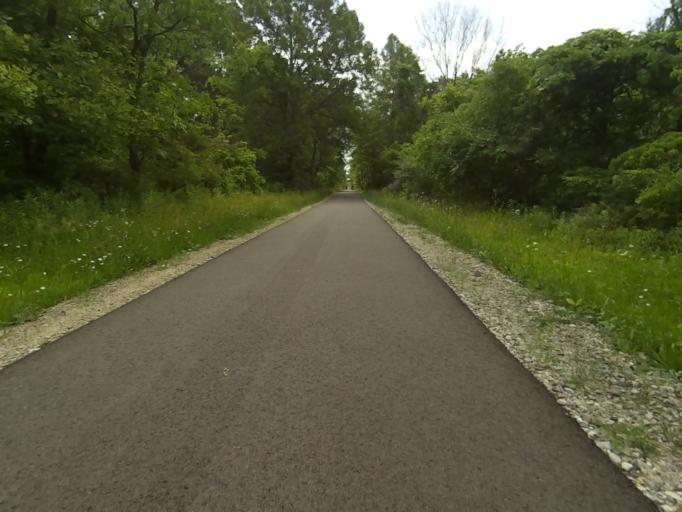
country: US
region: Ohio
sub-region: Summit County
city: Boston Heights
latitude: 41.2339
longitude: -81.4972
